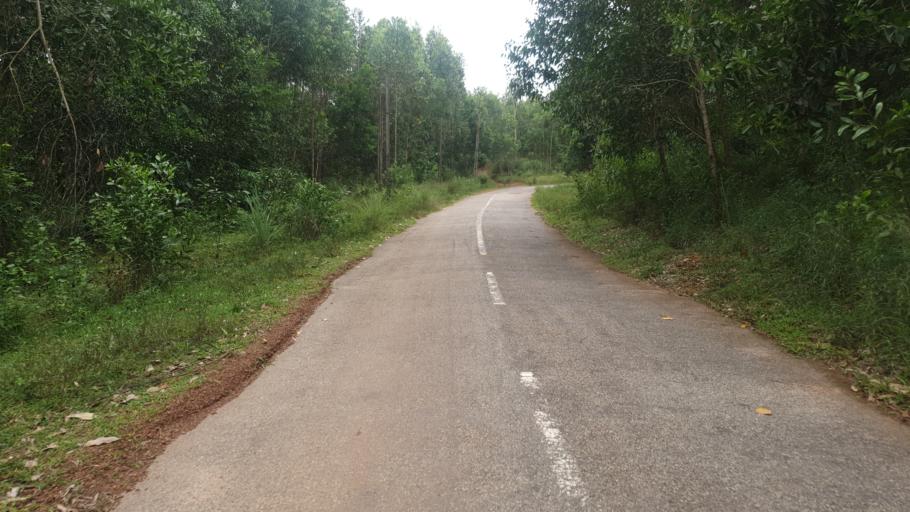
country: IN
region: Kerala
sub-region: Thiruvananthapuram
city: Nedumangad
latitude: 8.6360
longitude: 77.1110
